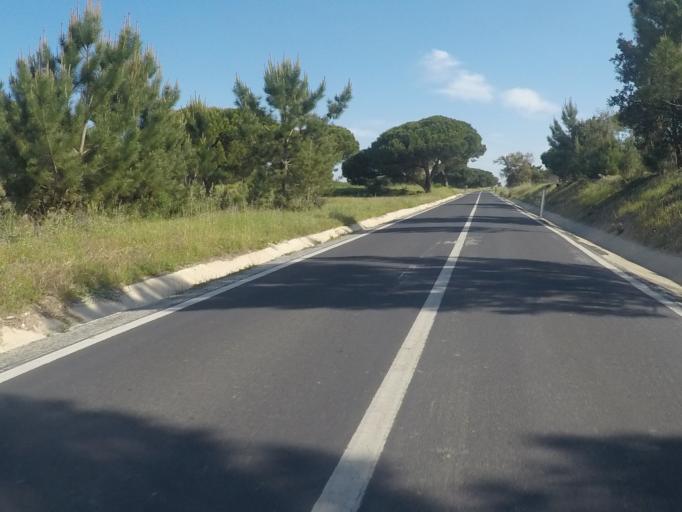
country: PT
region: Setubal
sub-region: Sesimbra
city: Sesimbra
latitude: 38.5112
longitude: -9.1451
